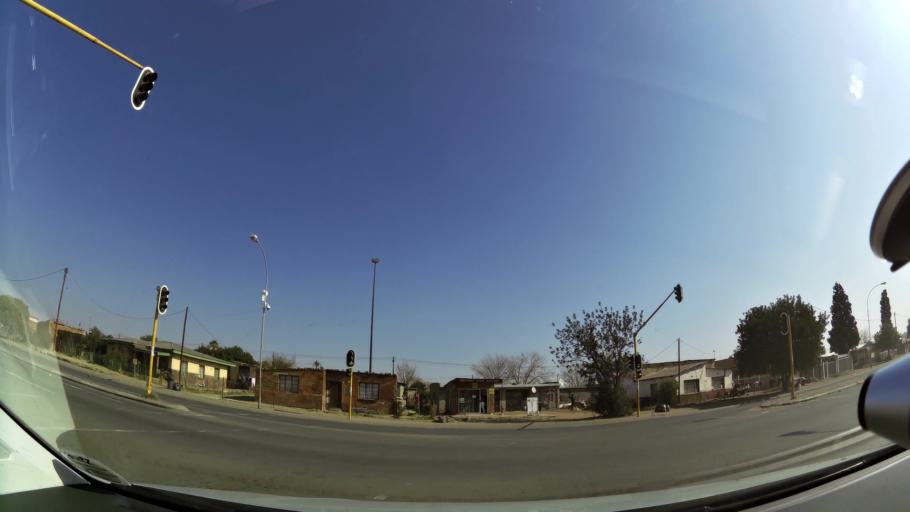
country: ZA
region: Orange Free State
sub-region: Mangaung Metropolitan Municipality
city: Bloemfontein
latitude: -29.1563
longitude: 26.2418
